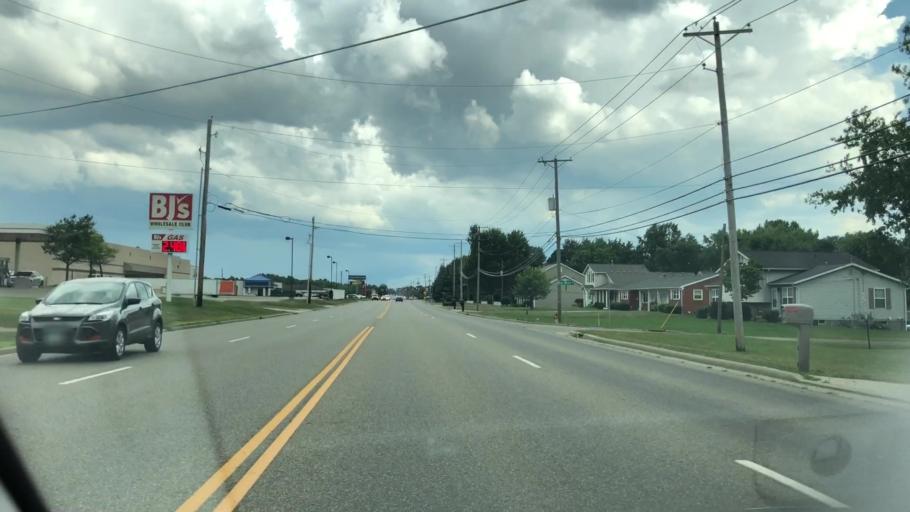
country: US
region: Ohio
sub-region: Stark County
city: North Canton
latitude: 40.8835
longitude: -81.4410
